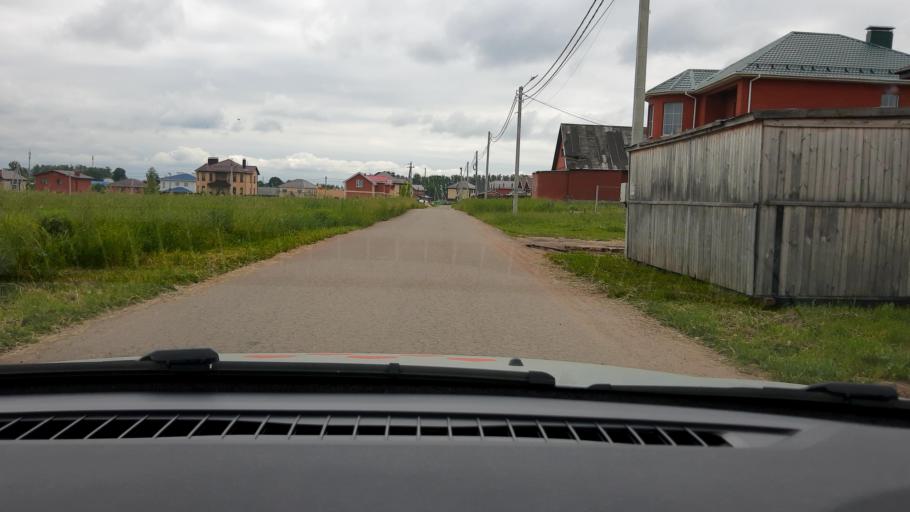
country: RU
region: Nizjnij Novgorod
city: Nizhniy Novgorod
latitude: 56.2181
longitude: 43.9667
